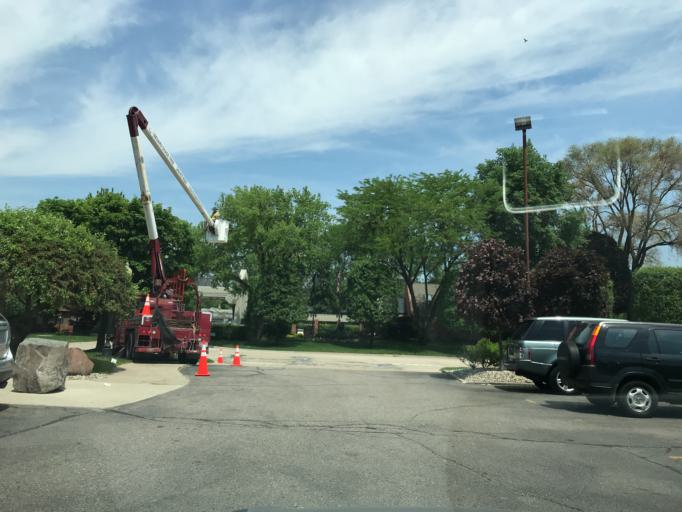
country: US
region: Michigan
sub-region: Oakland County
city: Southfield
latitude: 42.4727
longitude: -83.2347
